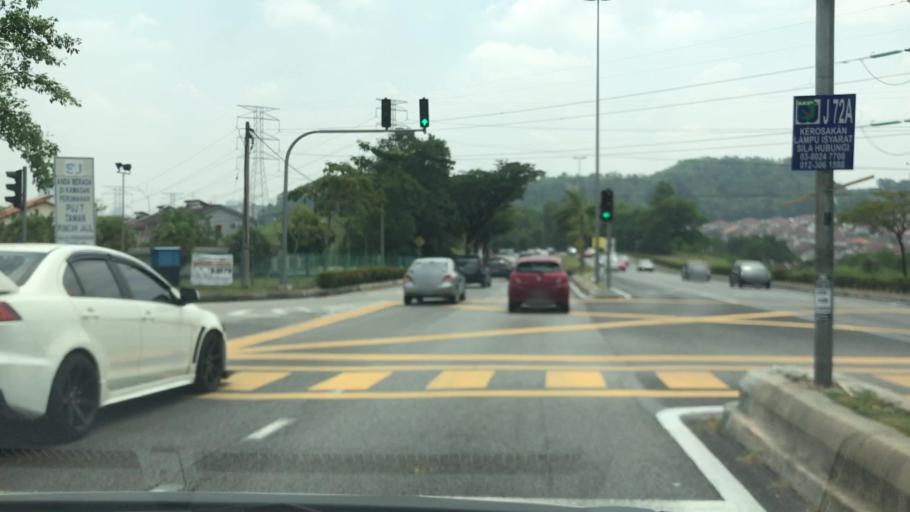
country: MY
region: Selangor
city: Kampong Baharu Balakong
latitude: 3.0275
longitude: 101.6804
